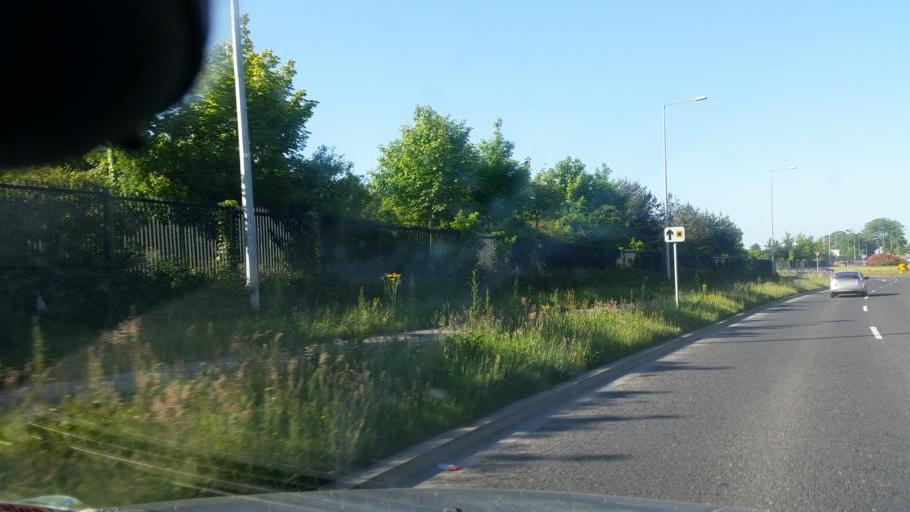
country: IE
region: Leinster
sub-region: Fingal County
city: Blanchardstown
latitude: 53.4170
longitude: -6.3828
